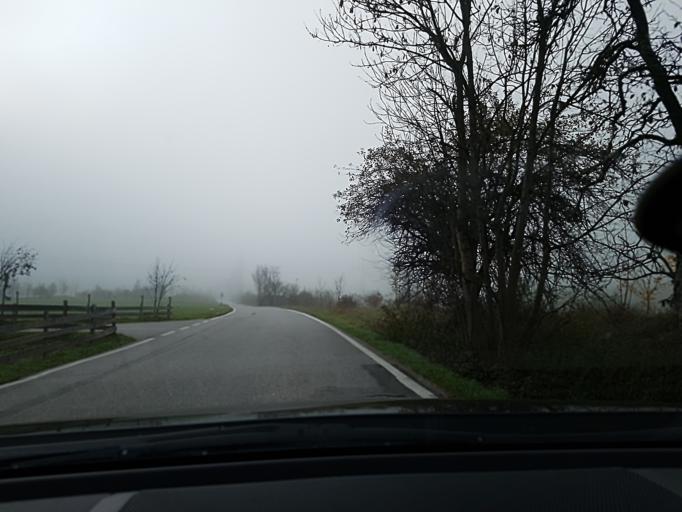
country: AT
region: Salzburg
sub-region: Politischer Bezirk Sankt Johann im Pongau
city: Bischofshofen
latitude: 47.3843
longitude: 13.2151
